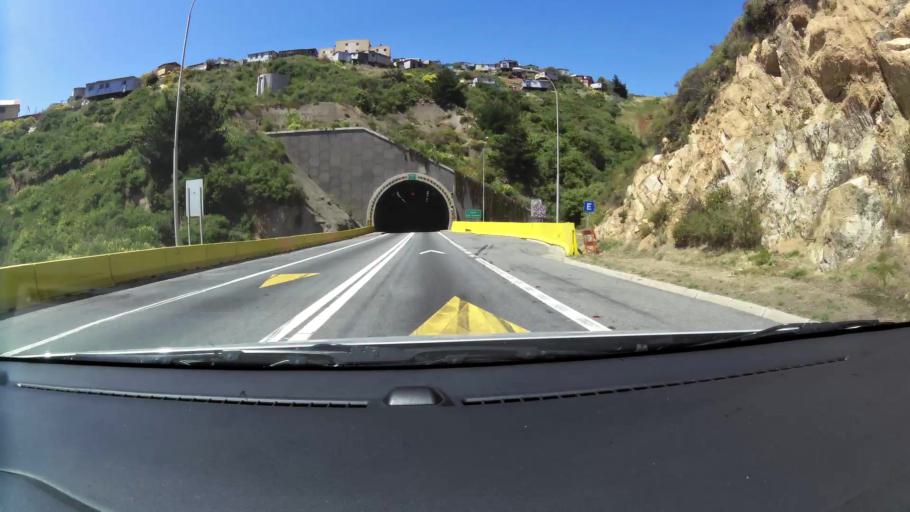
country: CL
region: Valparaiso
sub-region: Provincia de Valparaiso
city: Valparaiso
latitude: -33.0464
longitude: -71.6555
